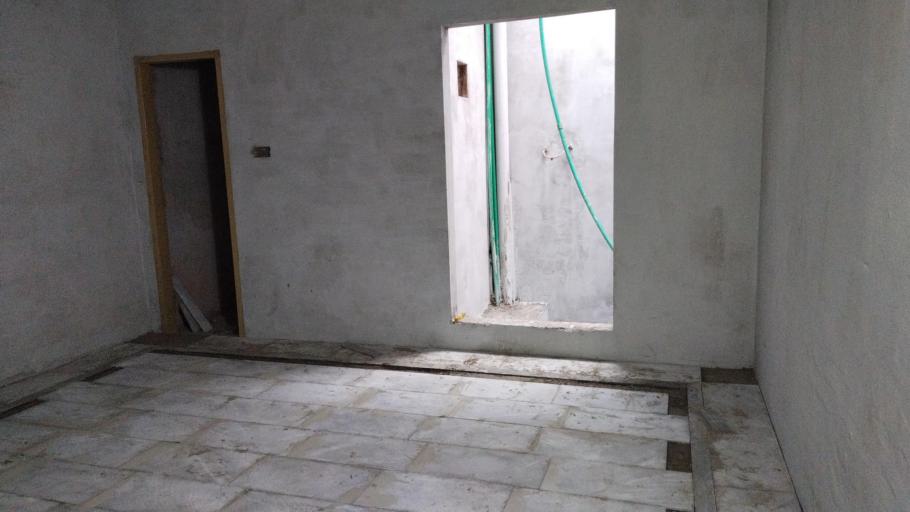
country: PK
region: Punjab
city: Lahore
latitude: 31.5839
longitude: 74.4151
